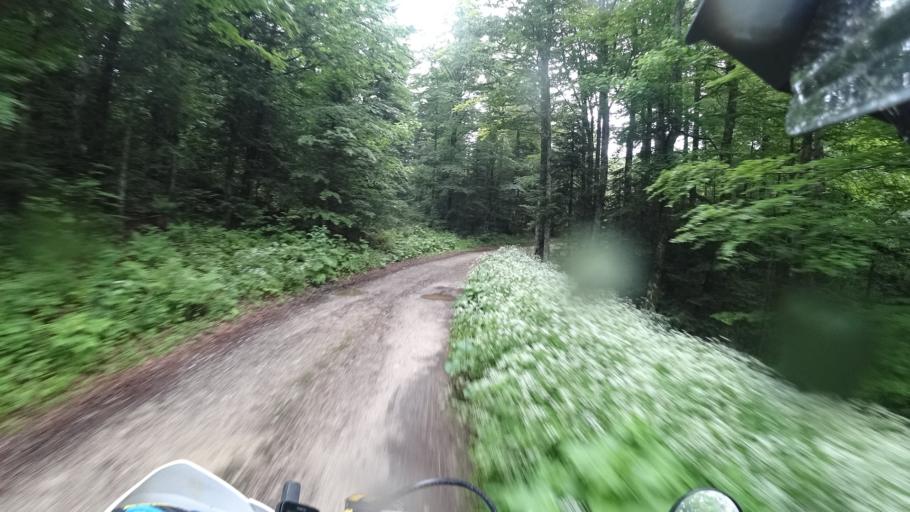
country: HR
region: Primorsko-Goranska
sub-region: Grad Delnice
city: Delnice
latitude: 45.3072
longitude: 14.9269
